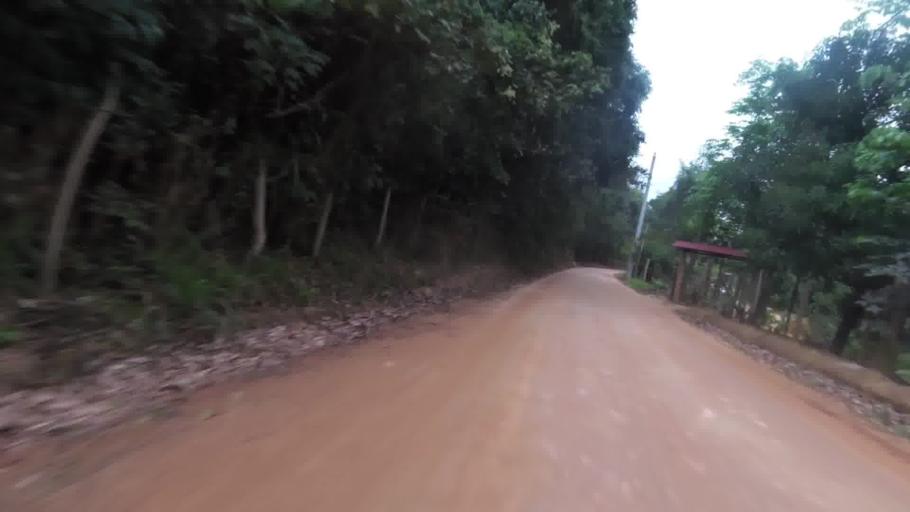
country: BR
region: Espirito Santo
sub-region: Alfredo Chaves
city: Alfredo Chaves
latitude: -20.6905
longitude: -40.7106
